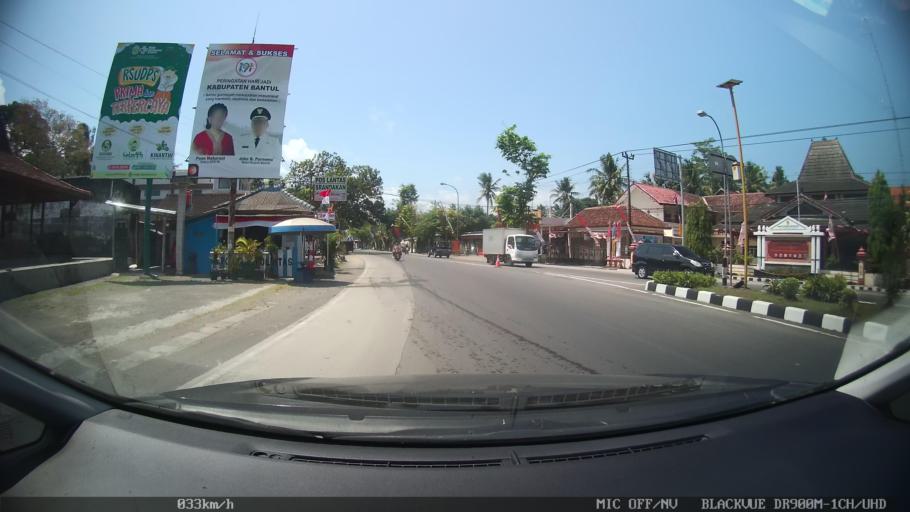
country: ID
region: Daerah Istimewa Yogyakarta
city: Srandakan
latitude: -7.9385
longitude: 110.2468
